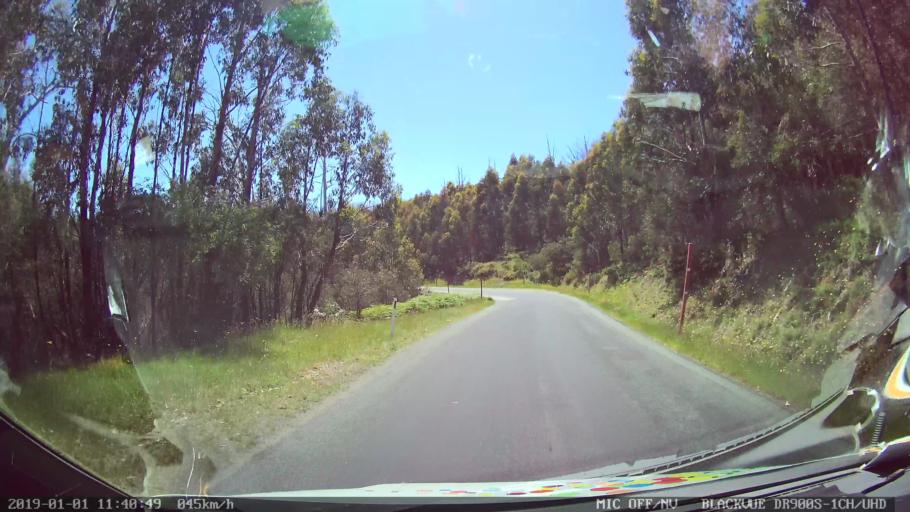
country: AU
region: New South Wales
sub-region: Snowy River
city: Jindabyne
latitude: -35.9176
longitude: 148.3883
